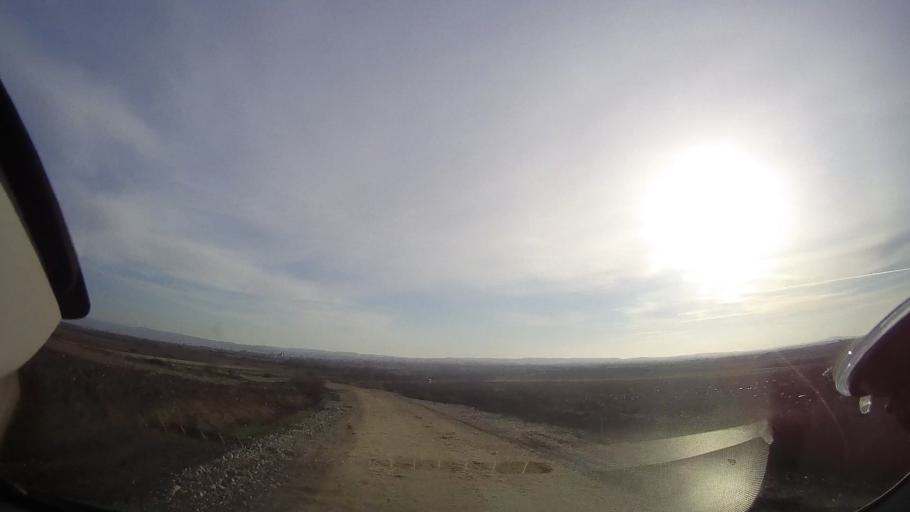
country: RO
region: Bihor
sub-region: Comuna Tileagd
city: Tileagd
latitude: 47.0942
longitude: 22.1777
